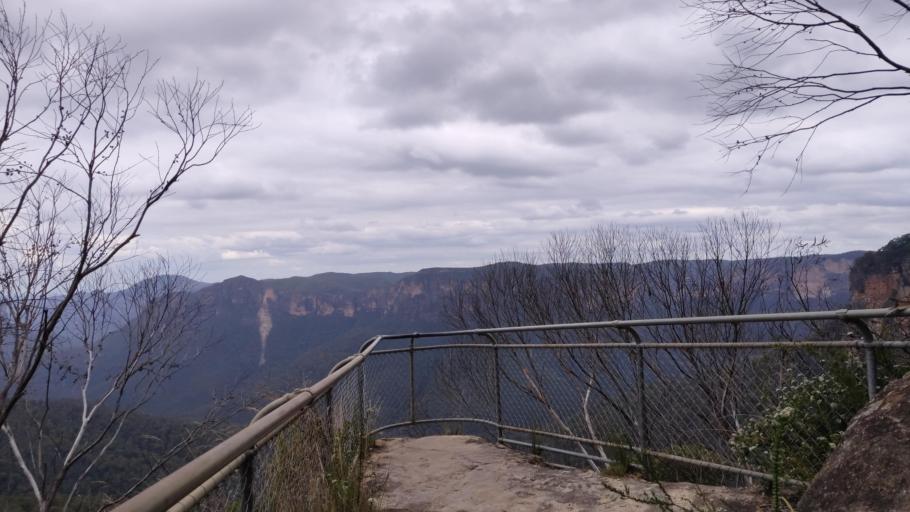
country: AU
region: New South Wales
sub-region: Blue Mountains Municipality
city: Blackheath
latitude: -33.6267
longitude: 150.3118
